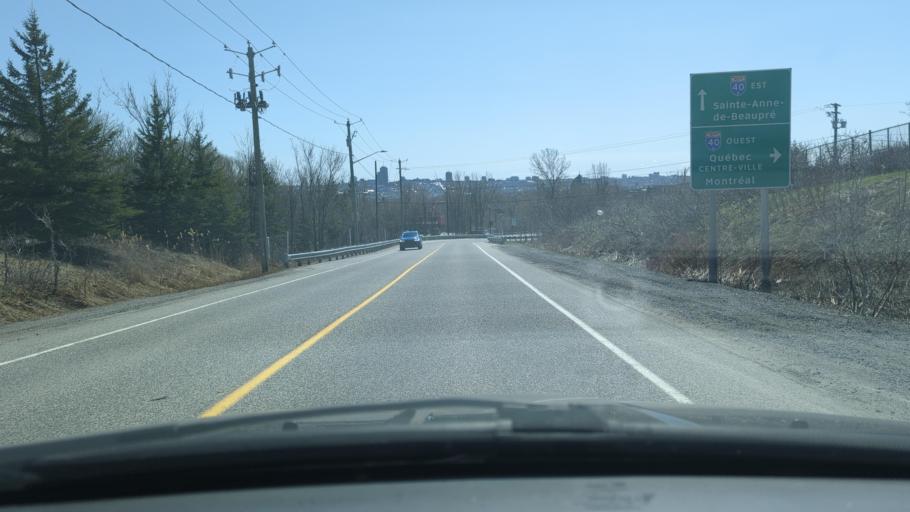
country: CA
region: Quebec
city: Quebec
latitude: 46.8567
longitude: -71.2158
